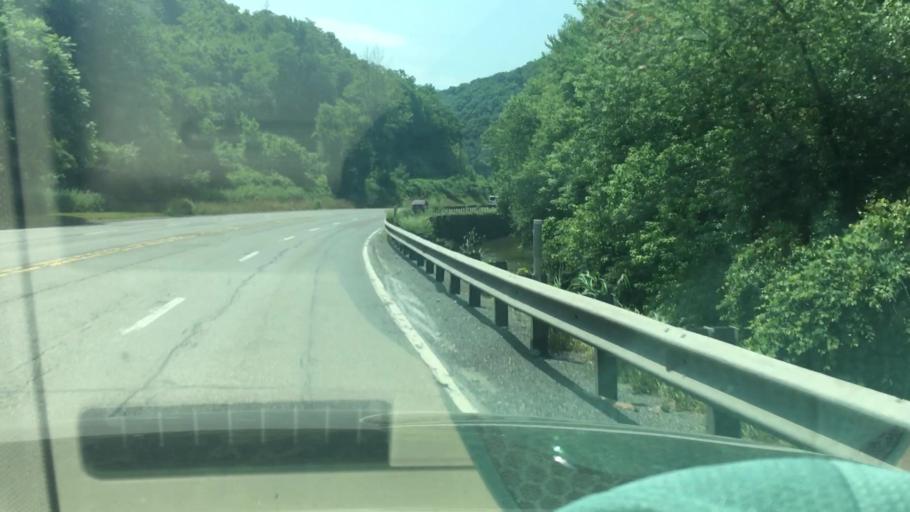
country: US
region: Pennsylvania
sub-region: Schuylkill County
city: Tamaqua
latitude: 40.7809
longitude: -75.9608
